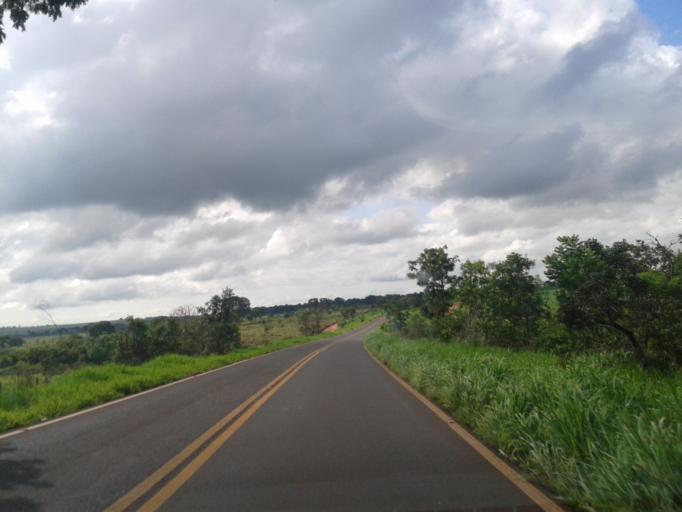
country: BR
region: Minas Gerais
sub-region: Ituiutaba
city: Ituiutaba
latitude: -19.0329
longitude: -49.7687
